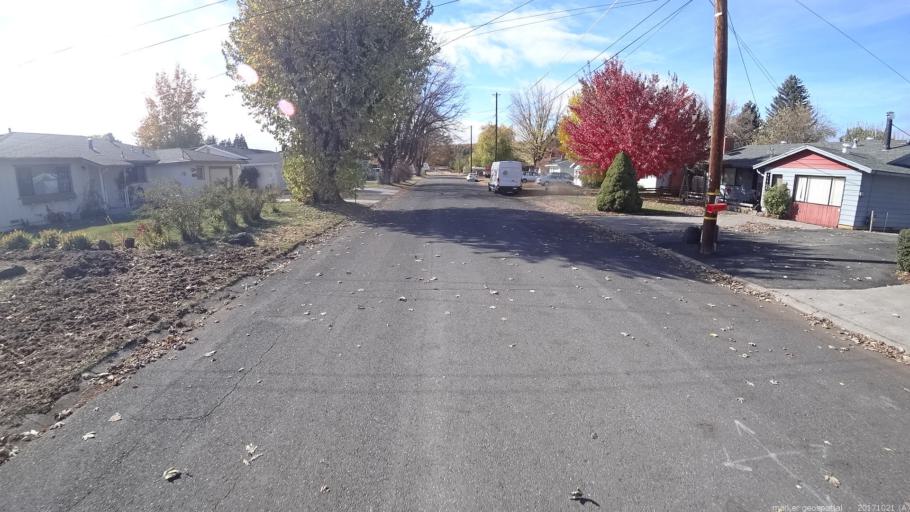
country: US
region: California
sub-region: Shasta County
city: Burney
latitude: 40.8841
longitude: -121.6629
